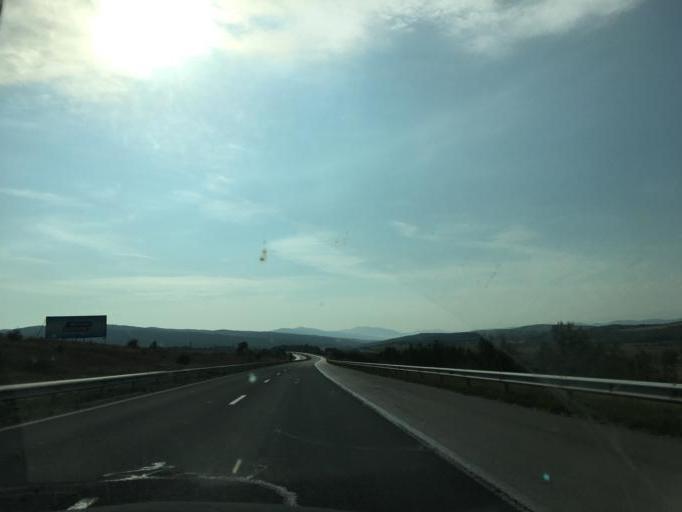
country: BG
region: Sofiya
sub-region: Obshtina Gorna Malina
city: Gorna Malina
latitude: 42.5427
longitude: 23.7167
